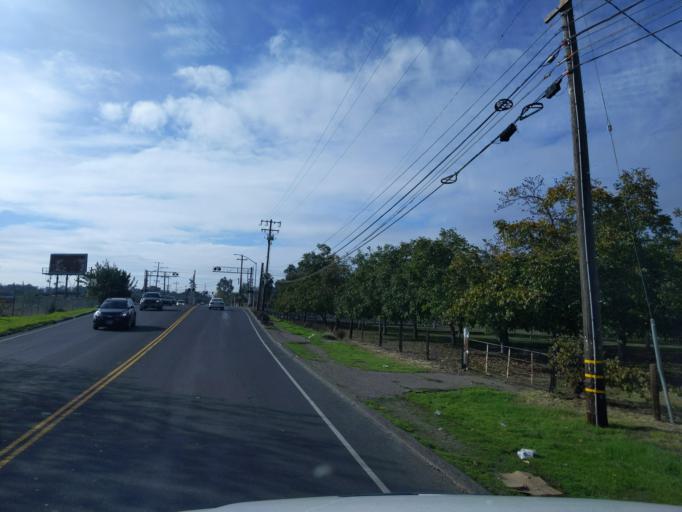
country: US
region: California
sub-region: San Joaquin County
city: August
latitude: 37.9847
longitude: -121.2811
